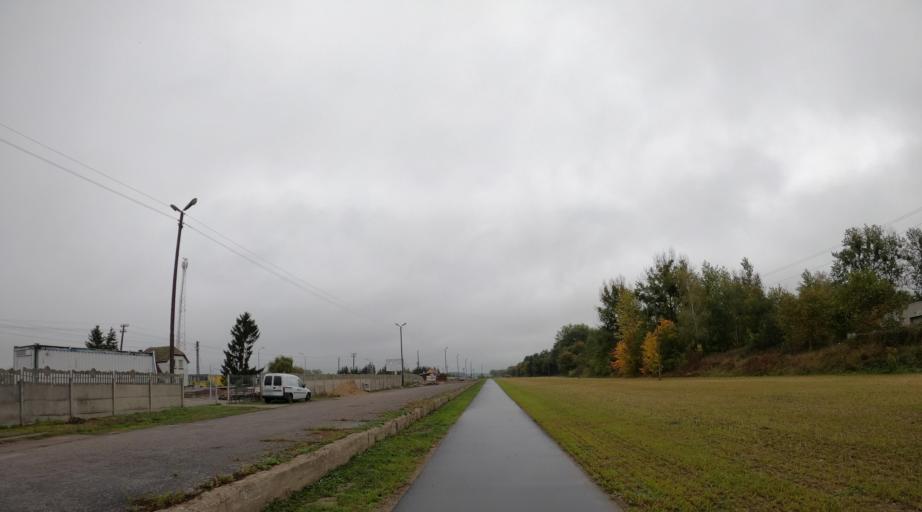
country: PL
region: West Pomeranian Voivodeship
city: Trzcinsko Zdroj
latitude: 52.9633
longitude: 14.6203
